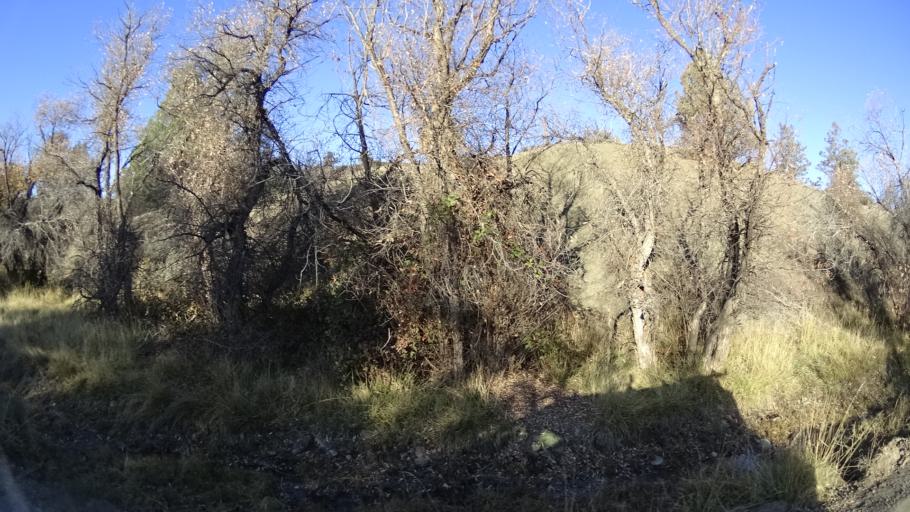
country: US
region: Oregon
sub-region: Jackson County
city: Ashland
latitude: 41.9913
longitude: -122.6234
